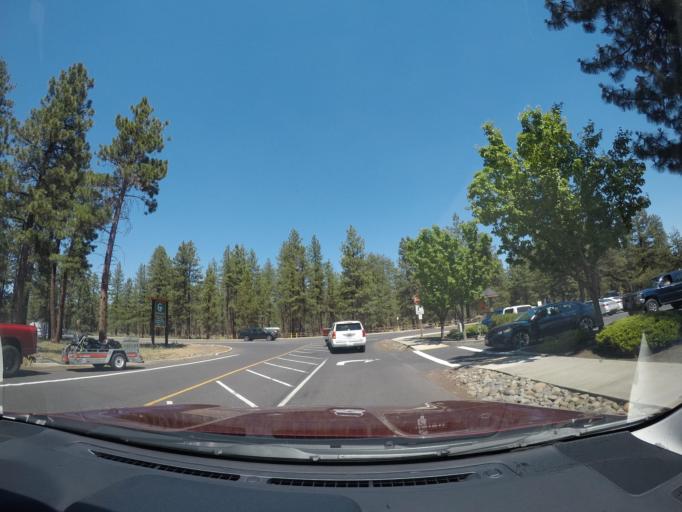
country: US
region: Oregon
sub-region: Deschutes County
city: Sisters
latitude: 44.2982
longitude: -121.5625
